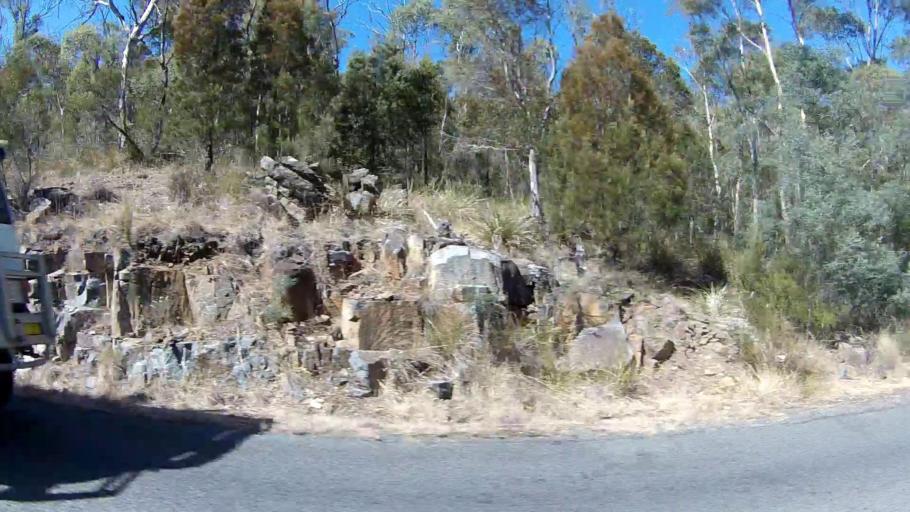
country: AU
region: Tasmania
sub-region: Sorell
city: Sorell
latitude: -42.5606
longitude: 147.8255
